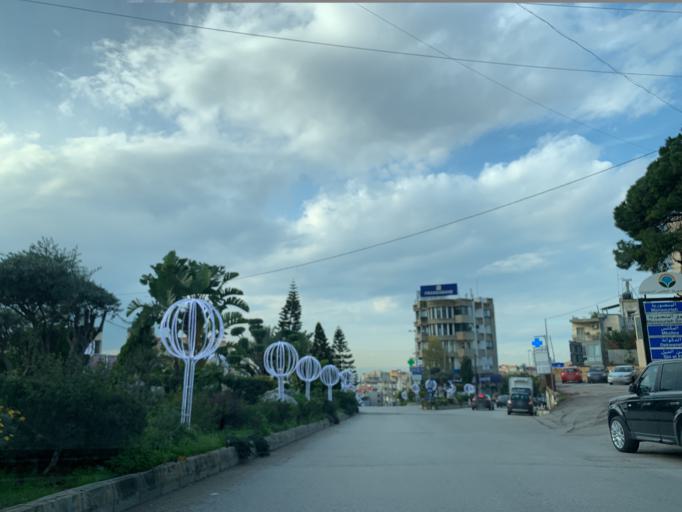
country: LB
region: Mont-Liban
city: Jdaidet el Matn
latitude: 33.8545
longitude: 35.5769
